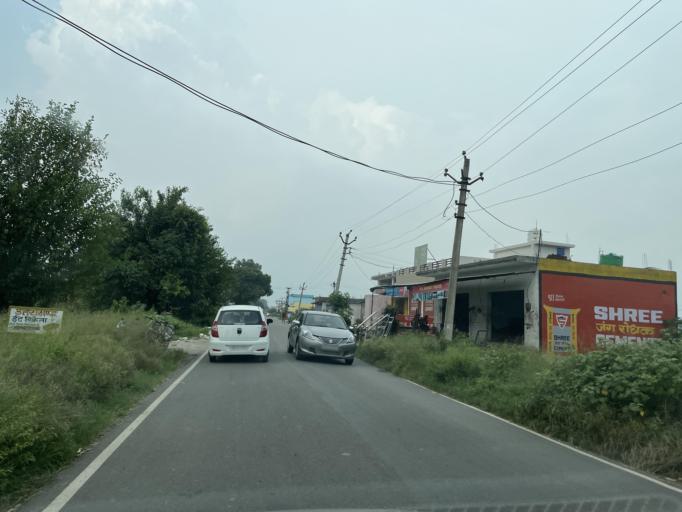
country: IN
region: Uttarakhand
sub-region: Naini Tal
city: Haldwani
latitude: 29.1847
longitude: 79.4758
